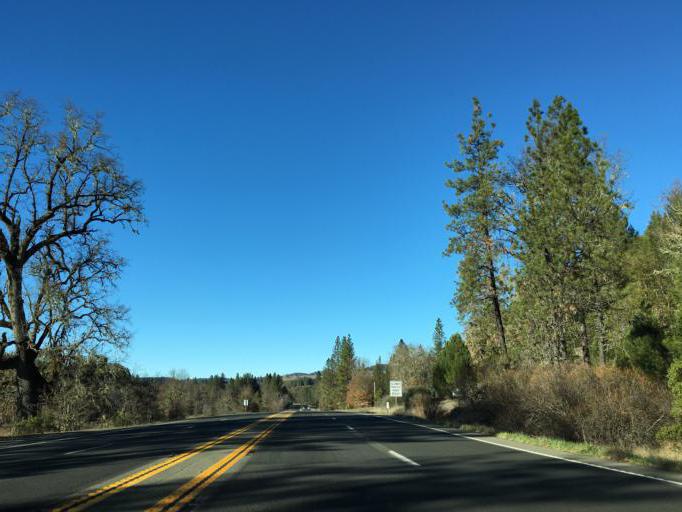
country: US
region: California
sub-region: Mendocino County
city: Laytonville
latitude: 39.7203
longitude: -123.5012
